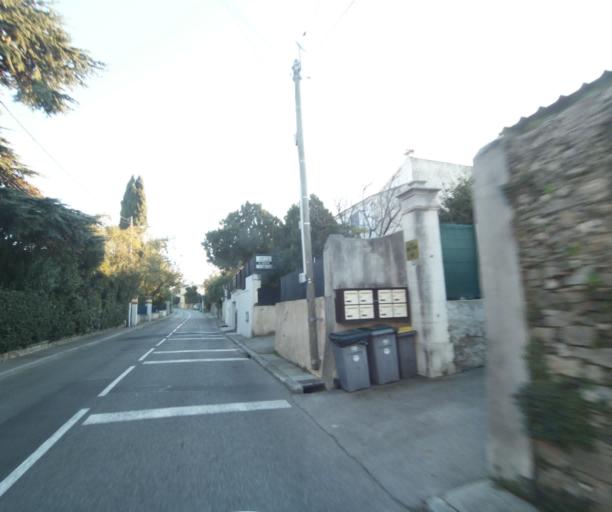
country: FR
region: Provence-Alpes-Cote d'Azur
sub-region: Departement des Alpes-Maritimes
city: Antibes
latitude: 43.5695
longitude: 7.1243
